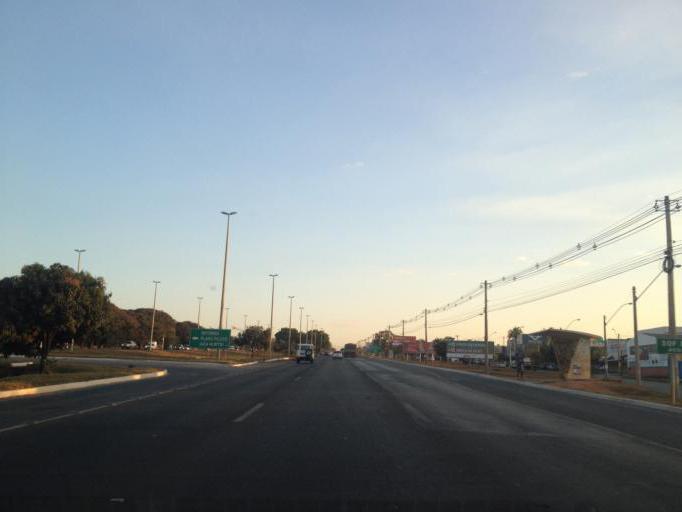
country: BR
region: Federal District
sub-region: Brasilia
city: Brasilia
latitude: -15.7482
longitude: -47.9222
